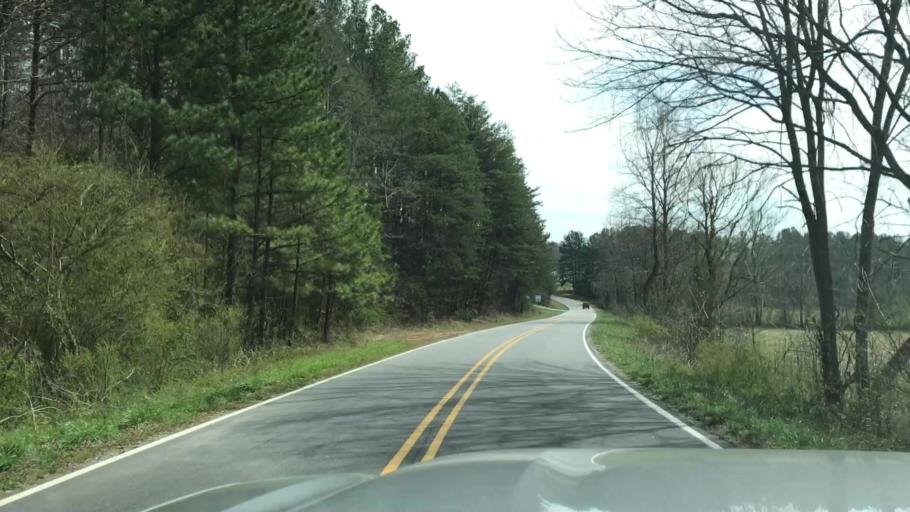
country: US
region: North Carolina
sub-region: Rutherford County
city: Spindale
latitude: 35.4467
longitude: -81.8797
